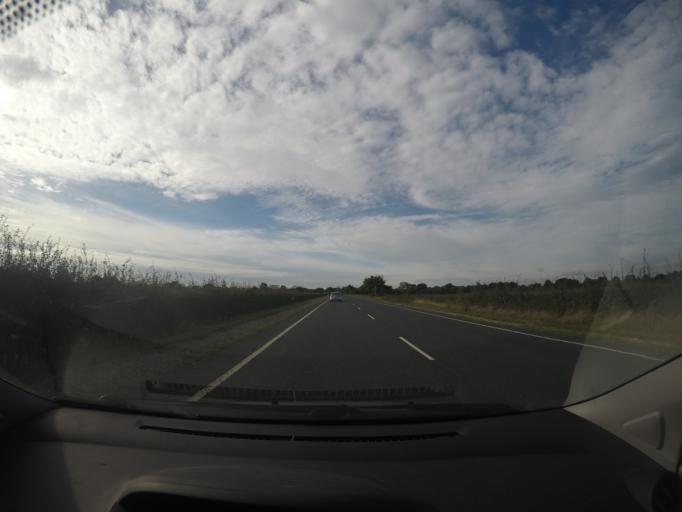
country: GB
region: England
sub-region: North Yorkshire
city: Riccall
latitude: 53.8469
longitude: -1.0528
